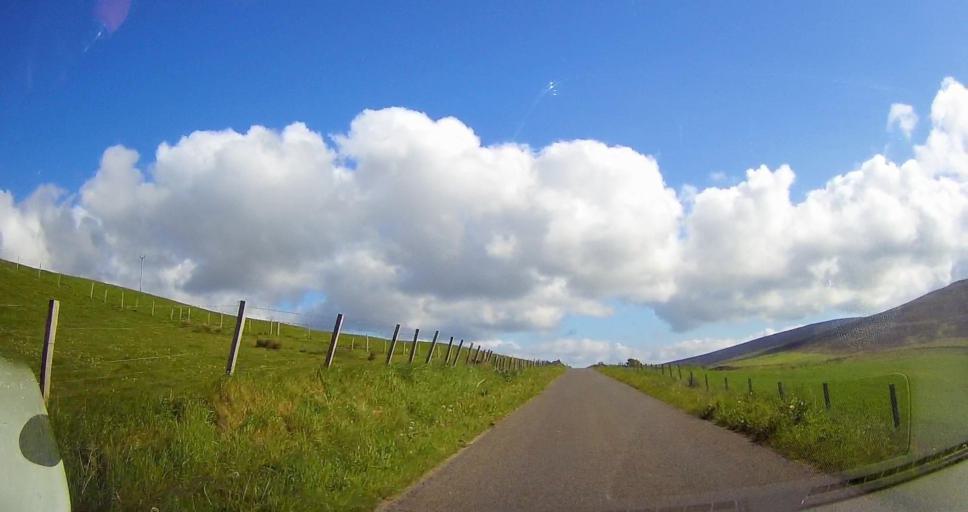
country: GB
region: Scotland
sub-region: Orkney Islands
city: Stromness
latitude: 58.9787
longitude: -3.1355
